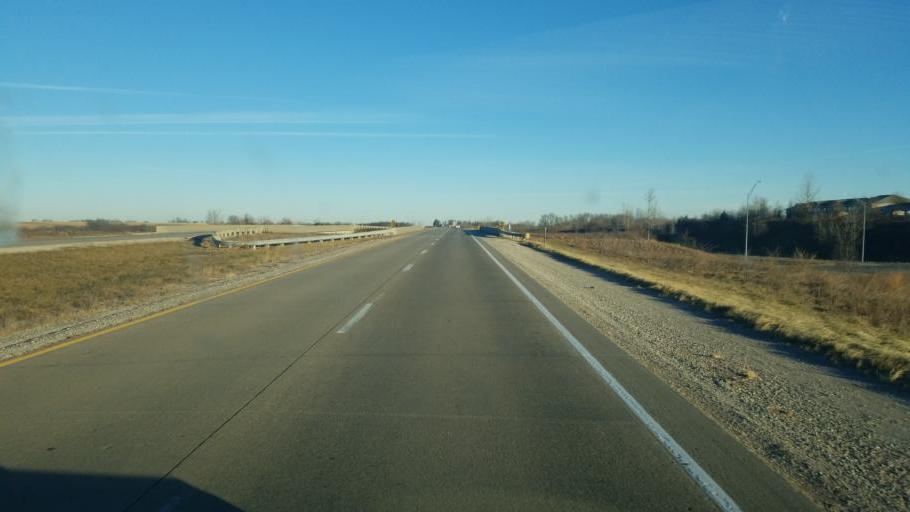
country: US
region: Iowa
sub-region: Mahaska County
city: Oskaloosa
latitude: 41.2951
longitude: -92.6745
